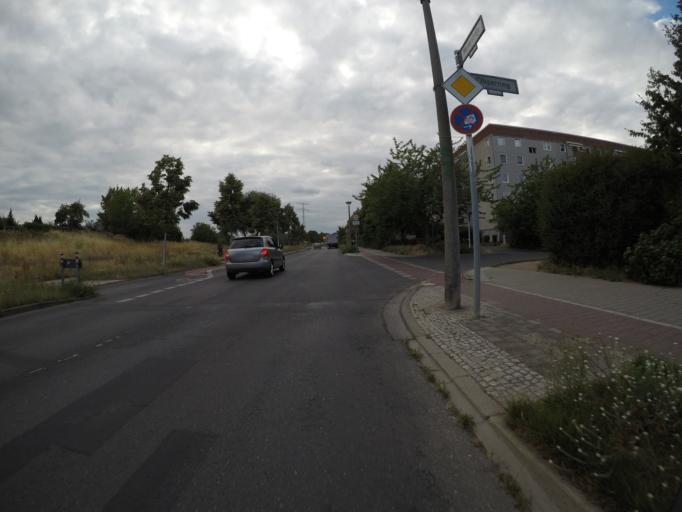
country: DE
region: Berlin
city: Kaulsdorf
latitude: 52.5189
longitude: 13.5997
